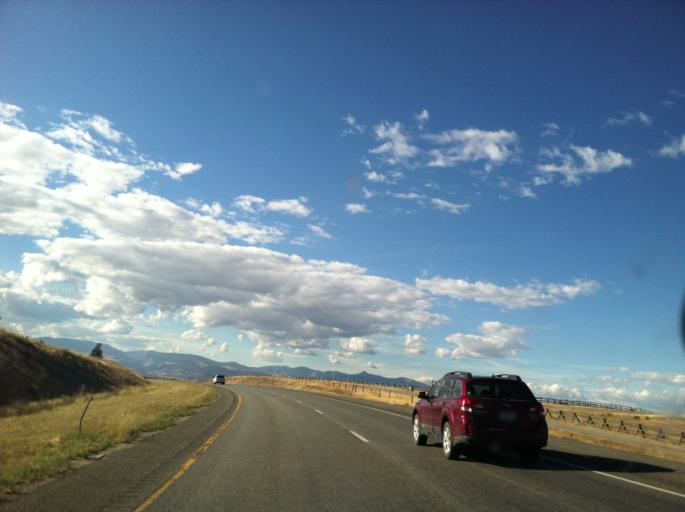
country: US
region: Montana
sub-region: Deer Lodge County
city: Warm Springs
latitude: 46.0396
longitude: -112.7356
